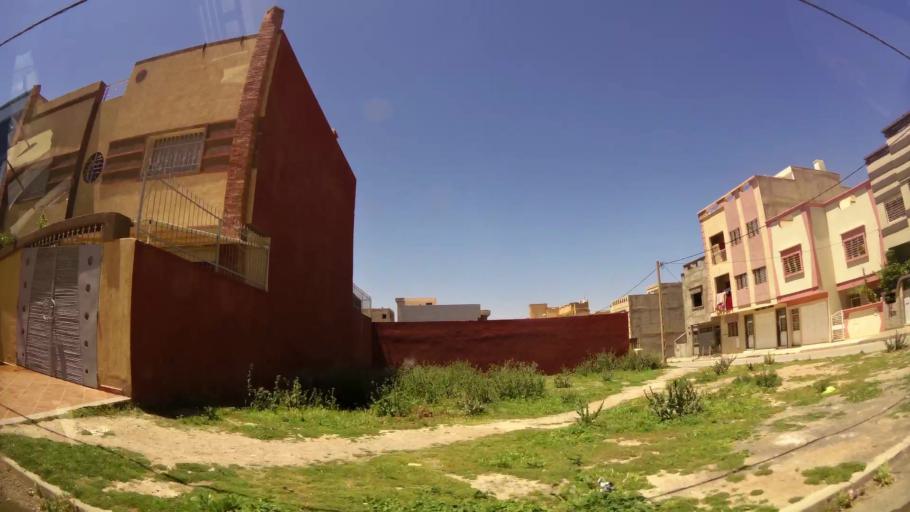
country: MA
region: Oriental
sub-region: Oujda-Angad
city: Oujda
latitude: 34.6672
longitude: -1.8789
